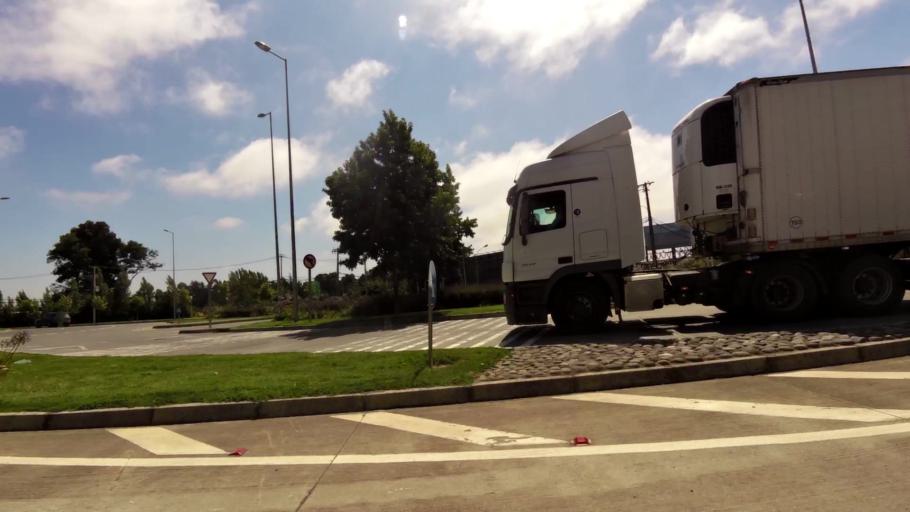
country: CL
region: Biobio
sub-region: Provincia de Concepcion
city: Concepcion
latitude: -36.7795
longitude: -73.0577
